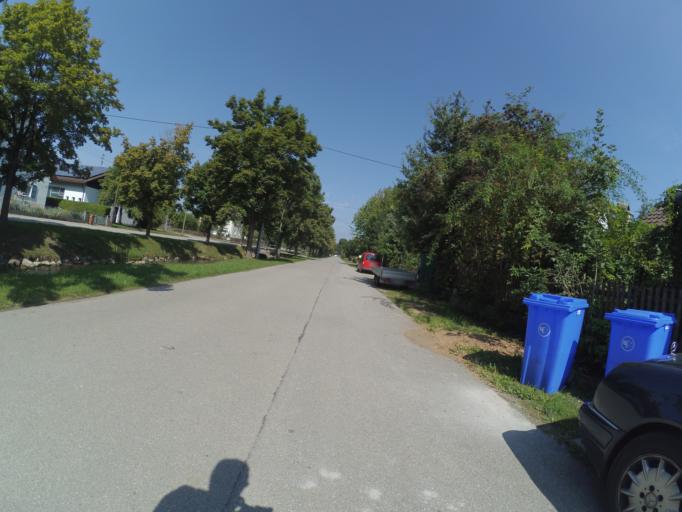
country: DE
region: Bavaria
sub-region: Swabia
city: Lamerdingen
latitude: 48.0911
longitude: 10.7376
